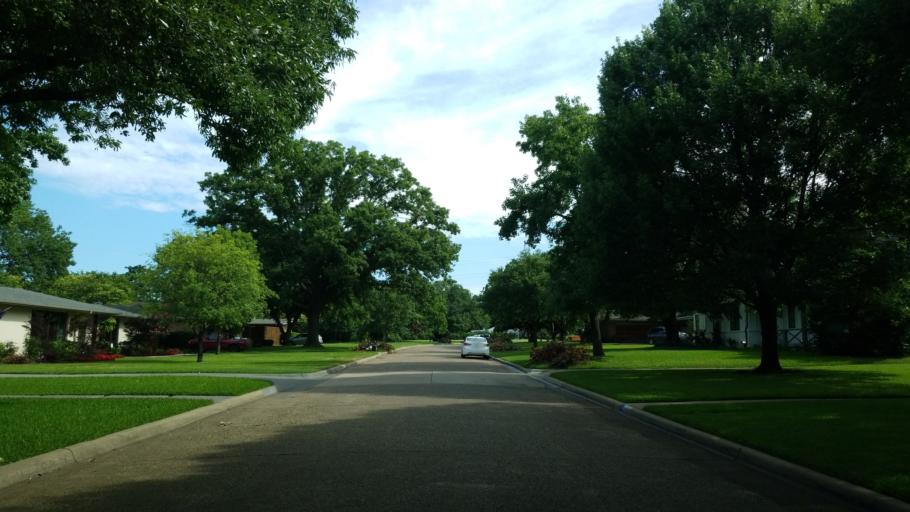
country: US
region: Texas
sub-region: Dallas County
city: University Park
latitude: 32.8981
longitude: -96.8401
